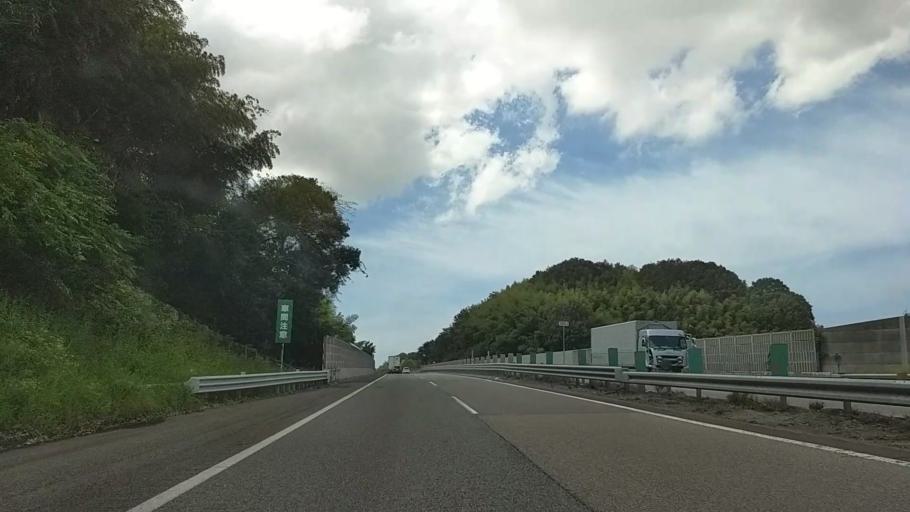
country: JP
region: Ishikawa
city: Kanazawa-shi
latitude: 36.6086
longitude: 136.6976
